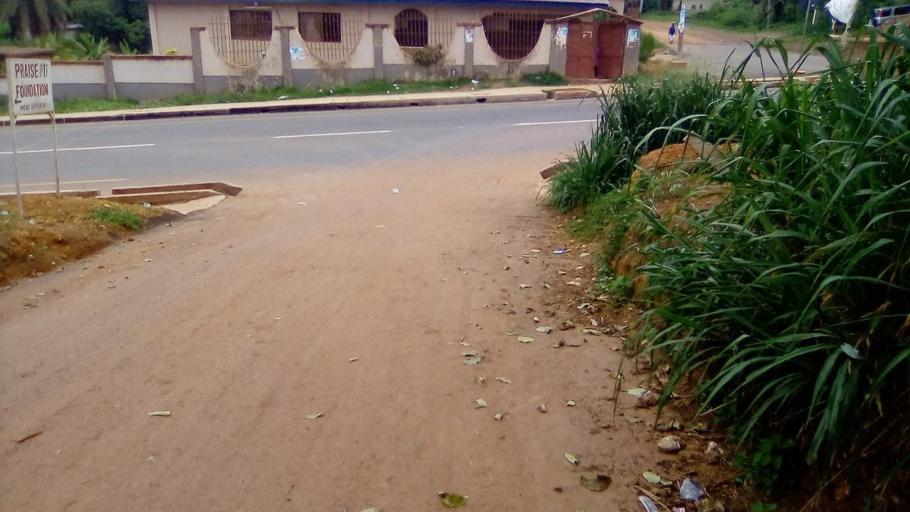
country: SL
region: Southern Province
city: Bo
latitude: 7.9570
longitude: -11.7258
